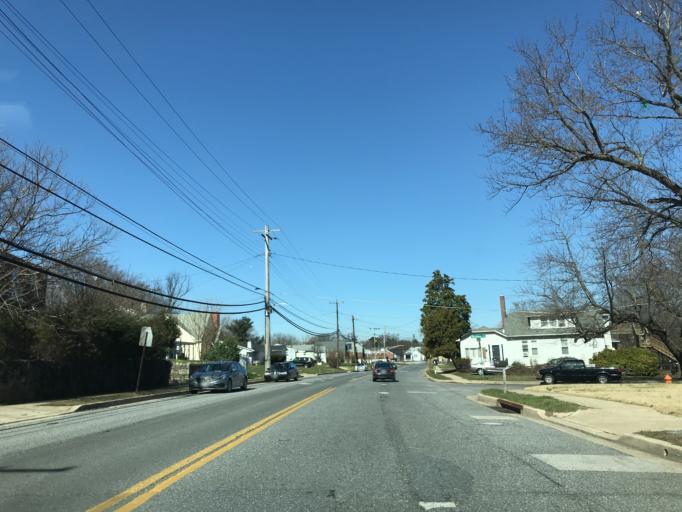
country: US
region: Maryland
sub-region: Baltimore County
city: Catonsville
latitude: 39.2909
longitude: -76.7279
